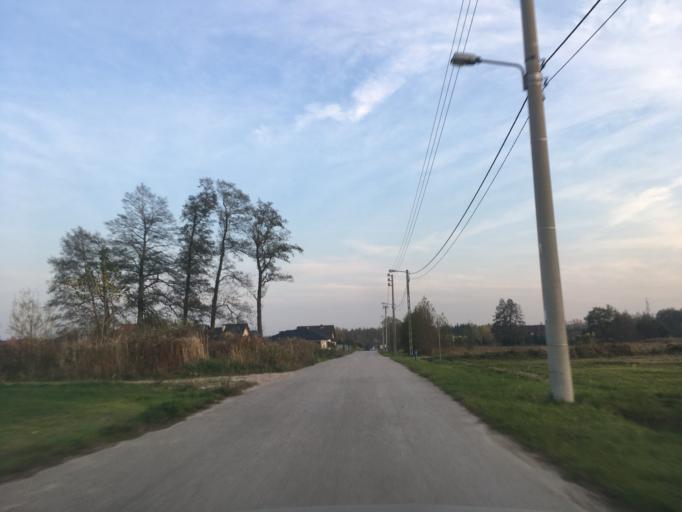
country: PL
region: Masovian Voivodeship
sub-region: Powiat piaseczynski
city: Lesznowola
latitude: 52.0495
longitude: 20.9273
